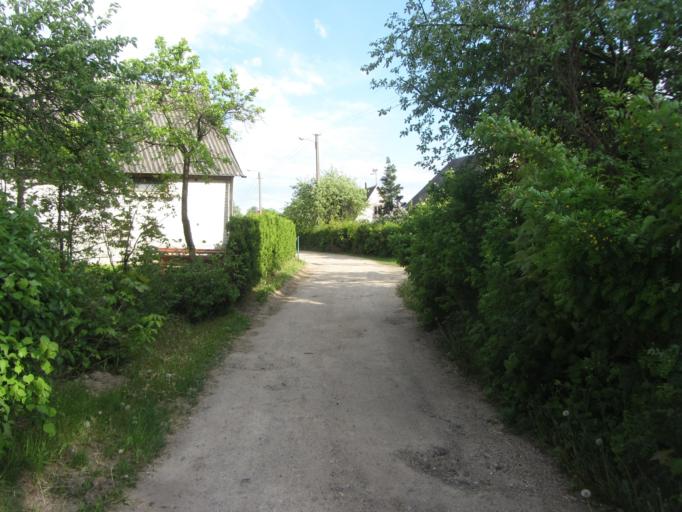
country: LT
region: Utenos apskritis
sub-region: Utena
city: Utena
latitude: 55.4978
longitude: 25.6047
